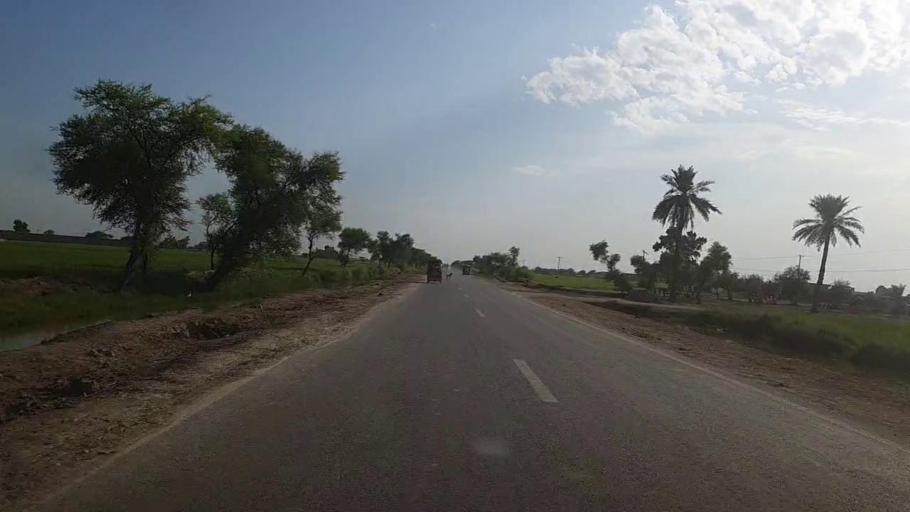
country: PK
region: Sindh
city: Thul
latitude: 28.2145
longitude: 68.7528
